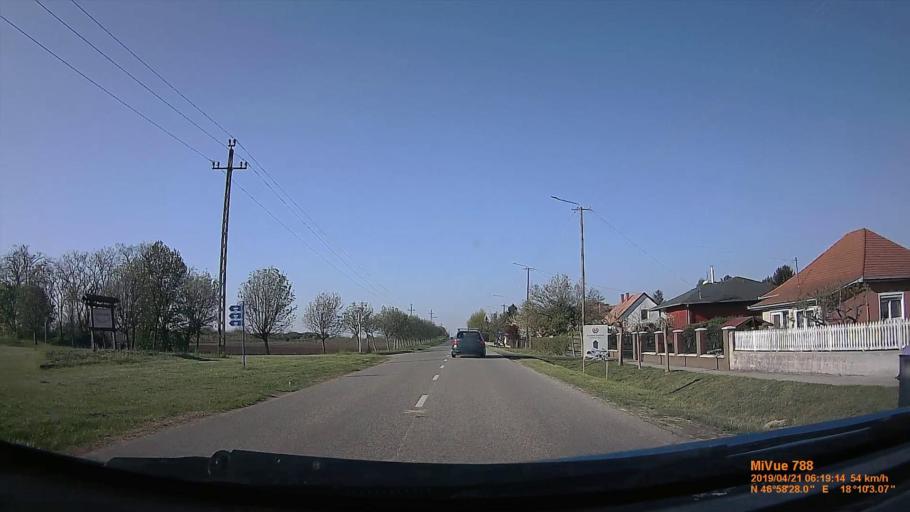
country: HU
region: Fejer
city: Lepseny
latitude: 46.9744
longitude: 18.1675
